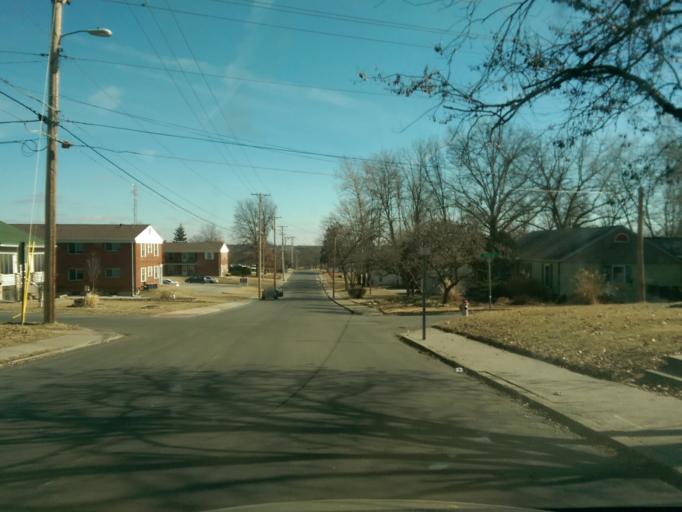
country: US
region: Missouri
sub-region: Boone County
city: Columbia
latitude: 38.9567
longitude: -92.3148
